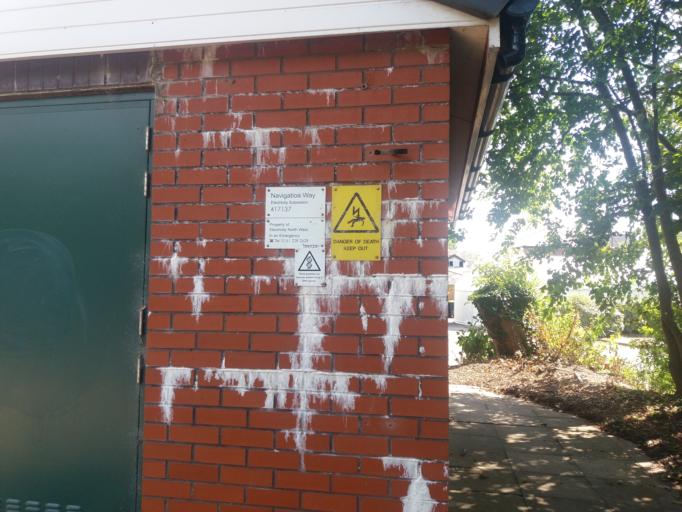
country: GB
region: England
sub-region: Lancashire
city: Preston
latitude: 53.7610
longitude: -2.7439
